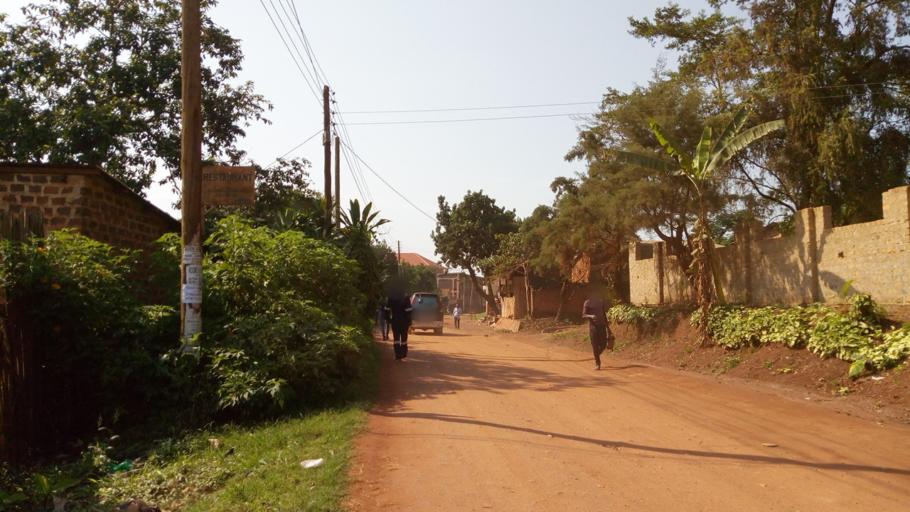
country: UG
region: Central Region
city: Kampala Central Division
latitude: 0.3423
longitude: 32.5649
